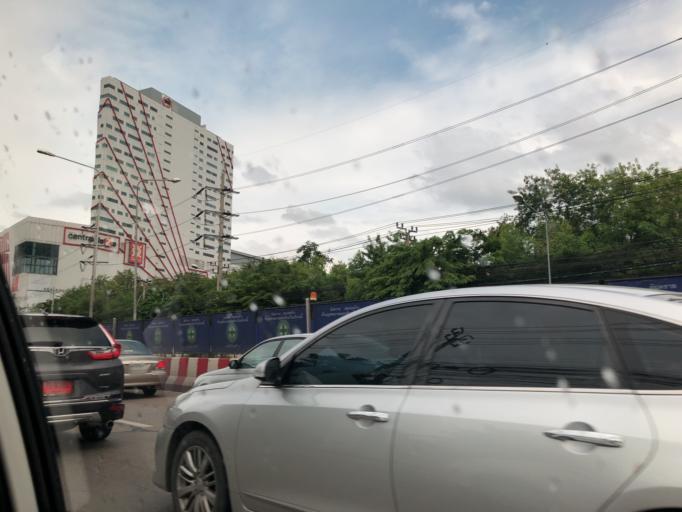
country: TH
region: Nonthaburi
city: Pak Kret
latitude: 13.9054
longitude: 100.5259
